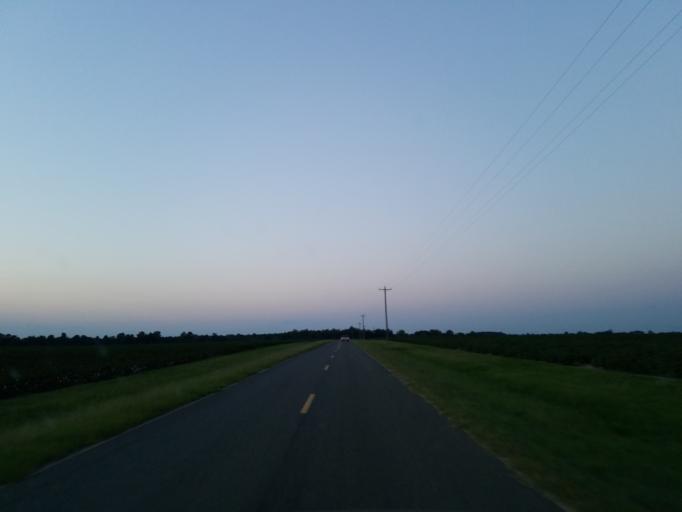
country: US
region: Georgia
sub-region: Dooly County
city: Unadilla
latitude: 32.2760
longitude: -83.7959
